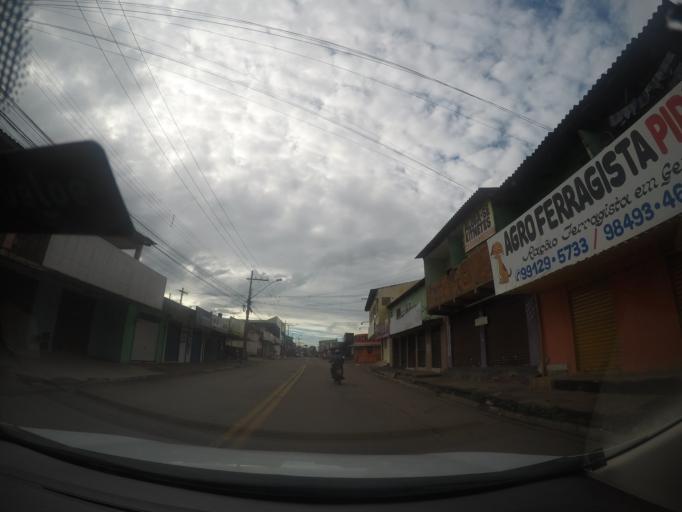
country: BR
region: Goias
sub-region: Goiania
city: Goiania
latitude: -16.6409
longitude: -49.3288
